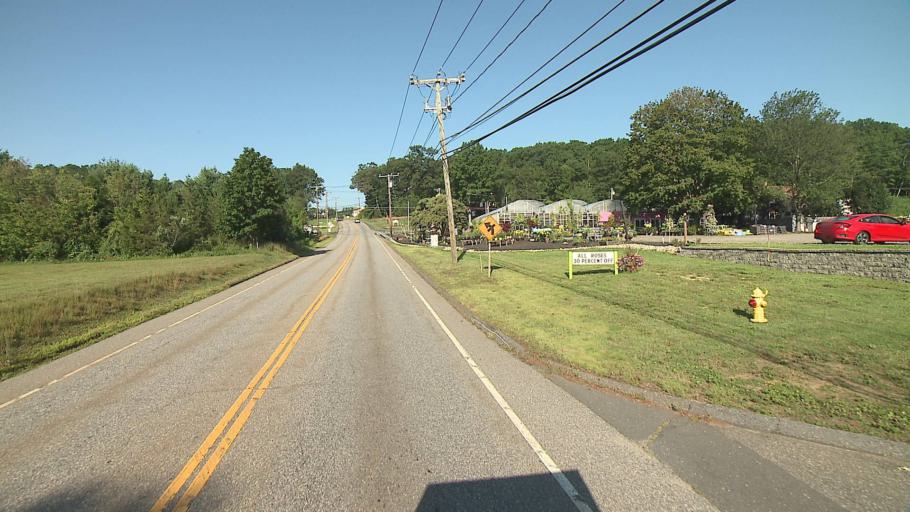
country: US
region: Connecticut
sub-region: Hartford County
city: Collinsville
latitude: 41.7700
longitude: -72.9608
